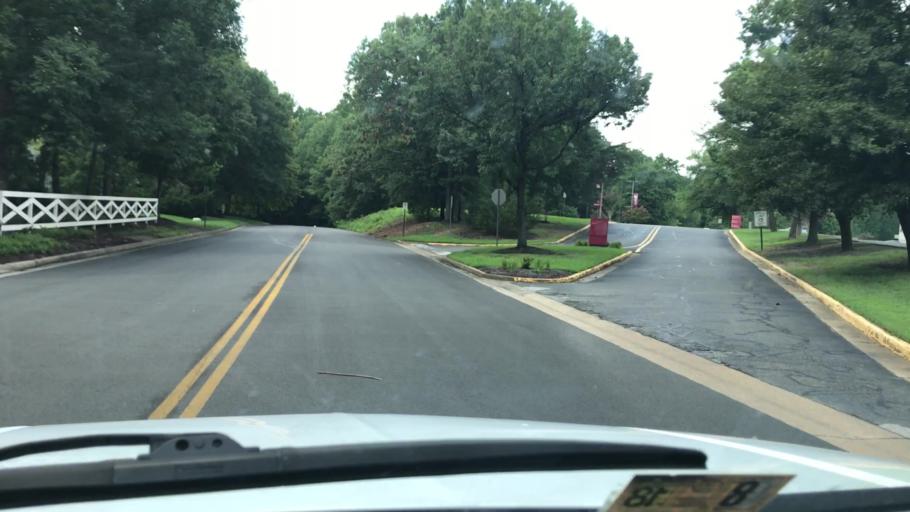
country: US
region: Virginia
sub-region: Henrico County
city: Lakeside
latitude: 37.6379
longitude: -77.4705
